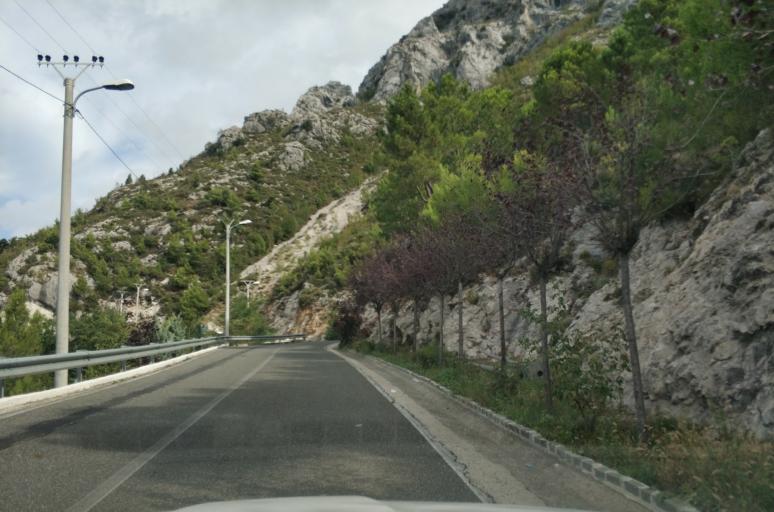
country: AL
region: Durres
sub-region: Rrethi i Krujes
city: Kruje
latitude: 41.5210
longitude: 19.7939
